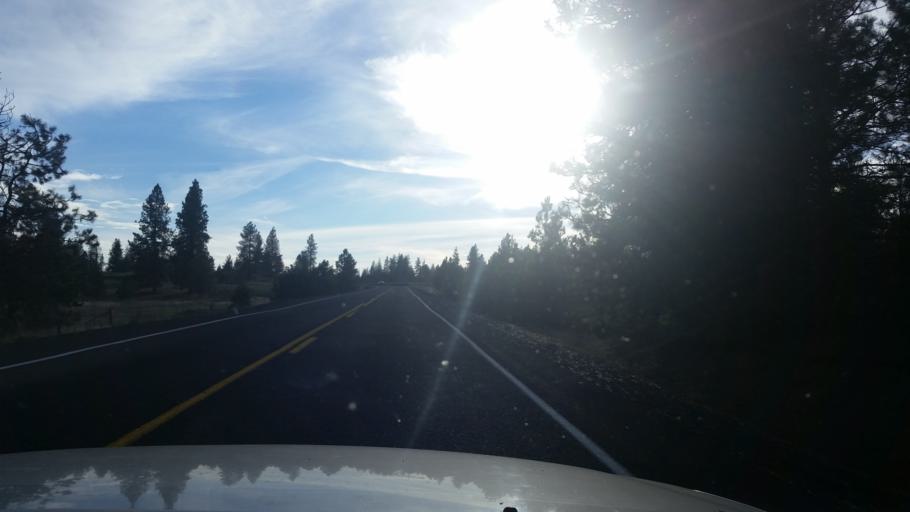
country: US
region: Washington
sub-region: Spokane County
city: Cheney
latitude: 47.3843
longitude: -117.5816
